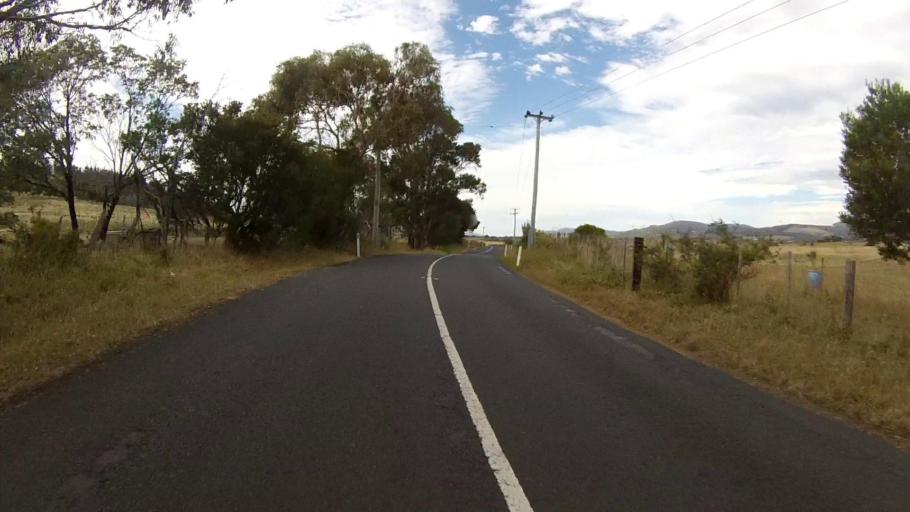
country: AU
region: Tasmania
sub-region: Clarence
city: Cambridge
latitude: -42.7238
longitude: 147.3965
